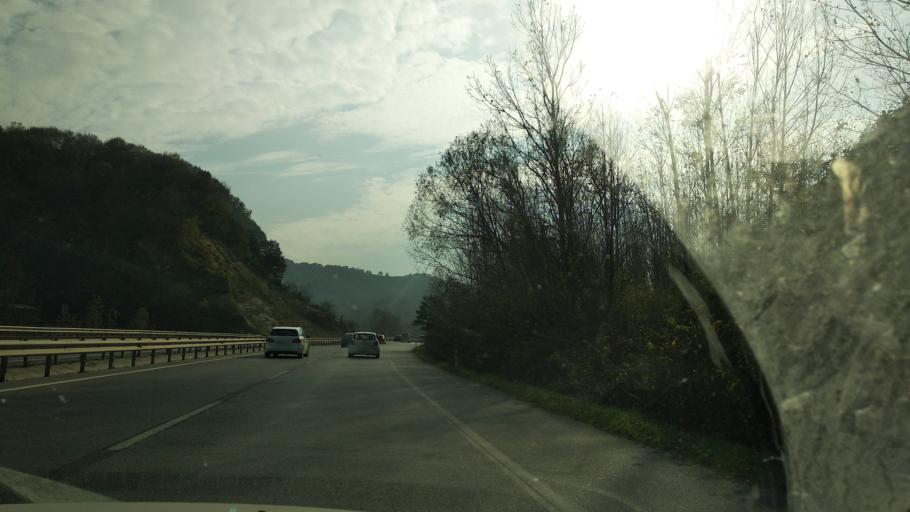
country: TR
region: Sakarya
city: Karasu
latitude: 41.0744
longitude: 30.6463
